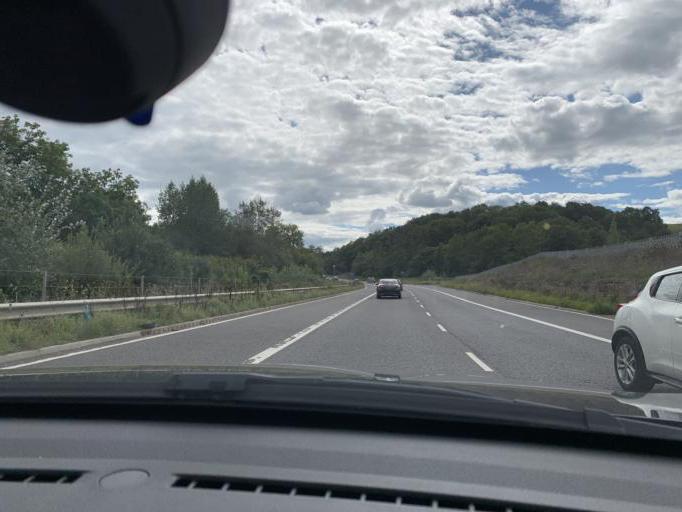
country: GB
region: England
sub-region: North Somerset
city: Long Ashton
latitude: 51.4250
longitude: -2.6356
